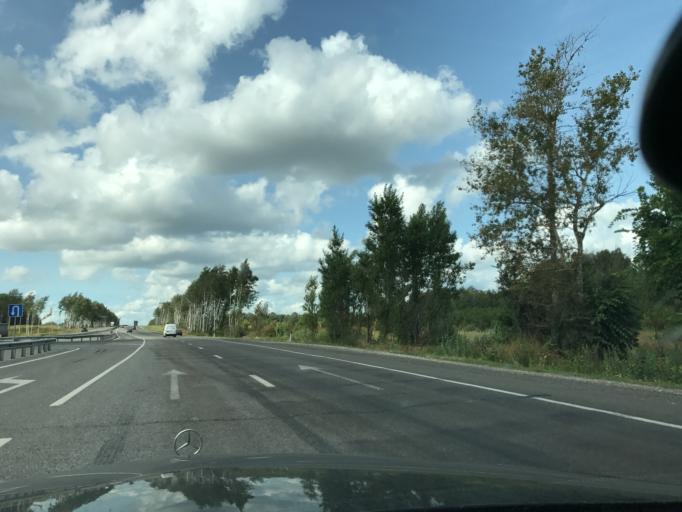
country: RU
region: Vladimir
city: Novovyazniki
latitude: 56.1933
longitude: 42.3804
